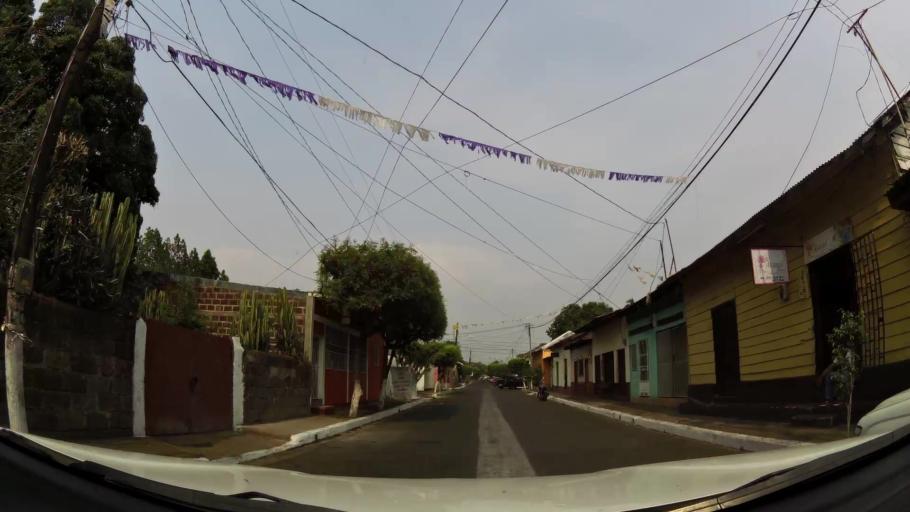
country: NI
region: Chinandega
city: Chinandega
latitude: 12.6284
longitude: -87.1267
